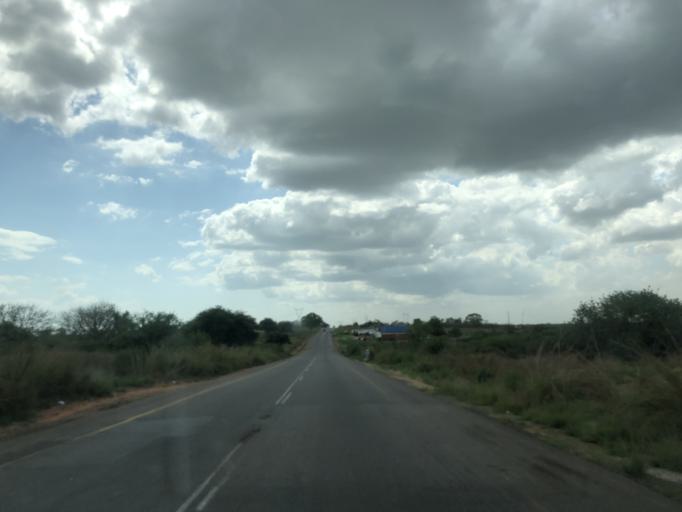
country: AO
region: Bengo
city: Caxito
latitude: -9.1190
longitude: 13.7313
